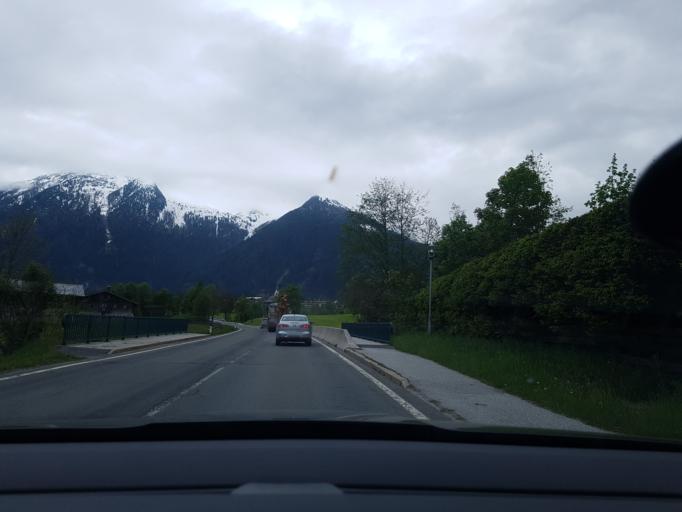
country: AT
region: Salzburg
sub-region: Politischer Bezirk Zell am See
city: Krimml
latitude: 47.2275
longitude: 12.1832
